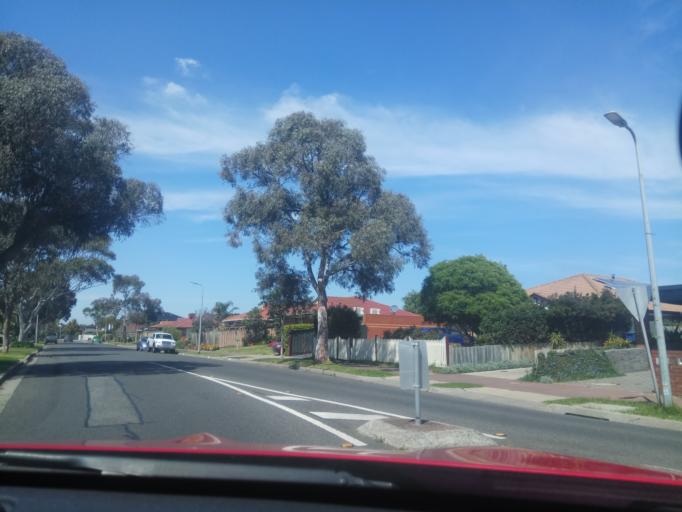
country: AU
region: Victoria
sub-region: Kingston
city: Aspendale Gardens
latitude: -38.0203
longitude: 145.1112
